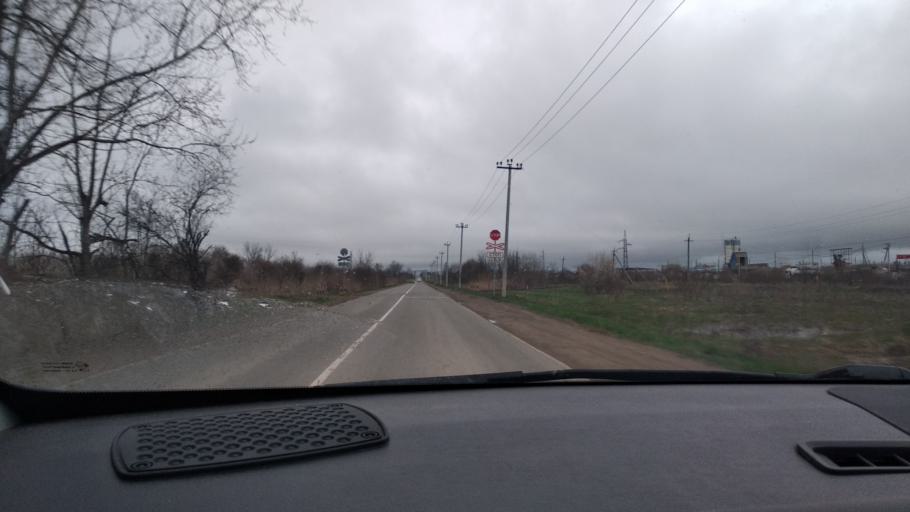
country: RU
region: Krasnodarskiy
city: Afipskiy
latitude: 44.8946
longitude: 38.8210
